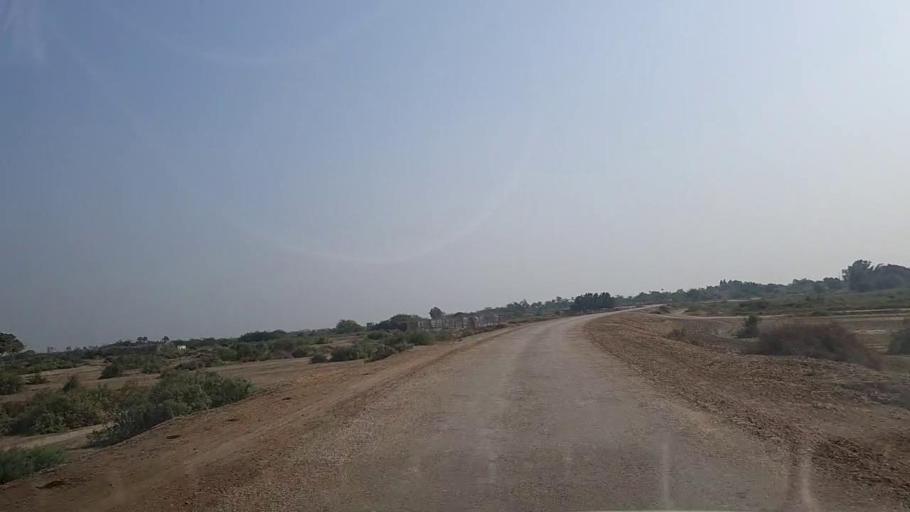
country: PK
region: Sindh
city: Keti Bandar
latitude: 24.2459
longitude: 67.6992
